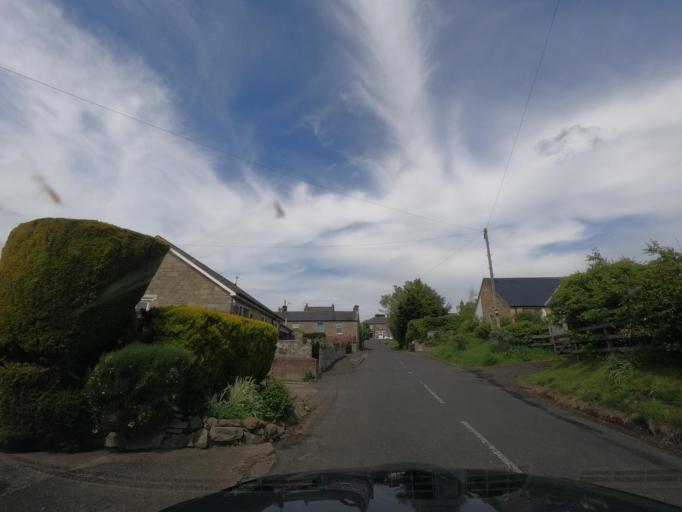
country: GB
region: England
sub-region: Northumberland
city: Whittingham
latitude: 55.4232
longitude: -1.8897
